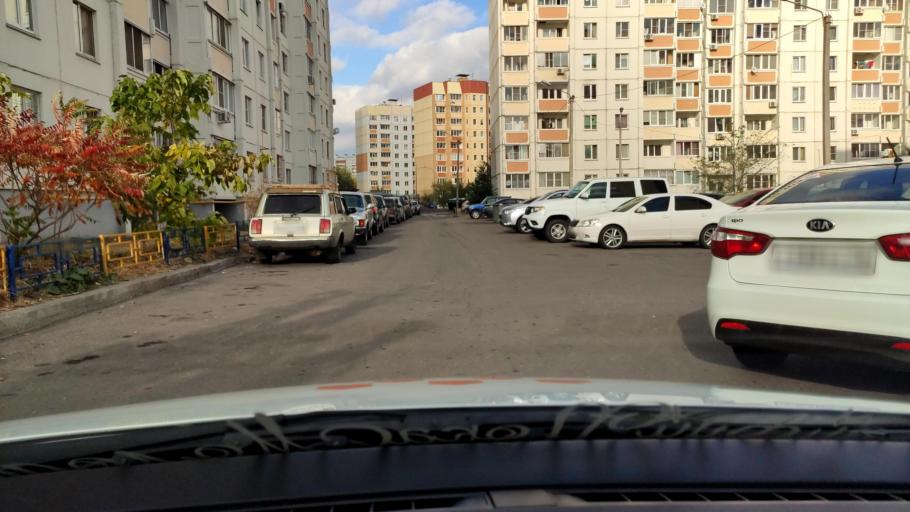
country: RU
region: Voronezj
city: Pridonskoy
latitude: 51.6787
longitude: 39.1210
